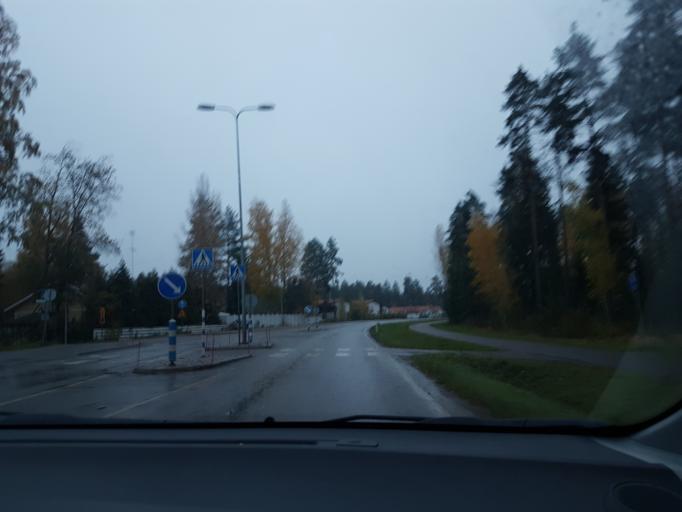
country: FI
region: Uusimaa
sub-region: Helsinki
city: Tuusula
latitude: 60.4006
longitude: 24.9844
